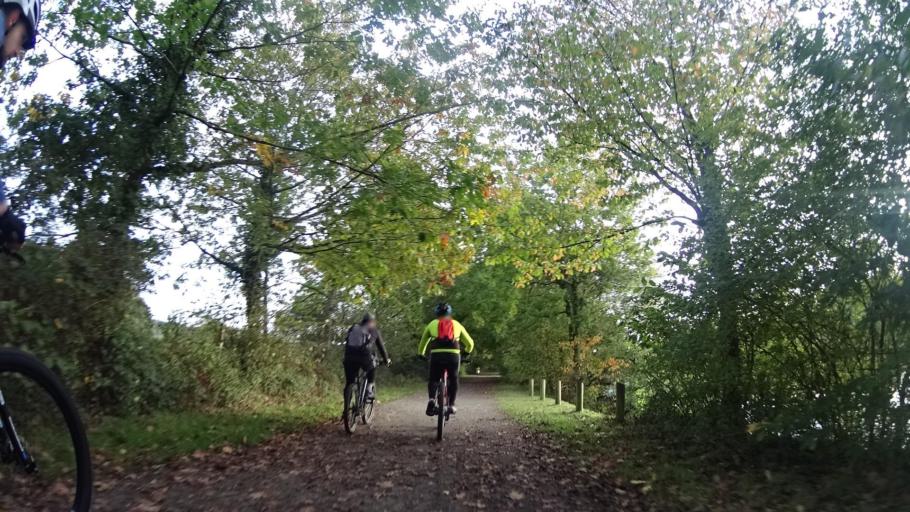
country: FR
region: Brittany
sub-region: Departement des Cotes-d'Armor
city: Evran
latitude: 48.3765
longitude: -2.0007
